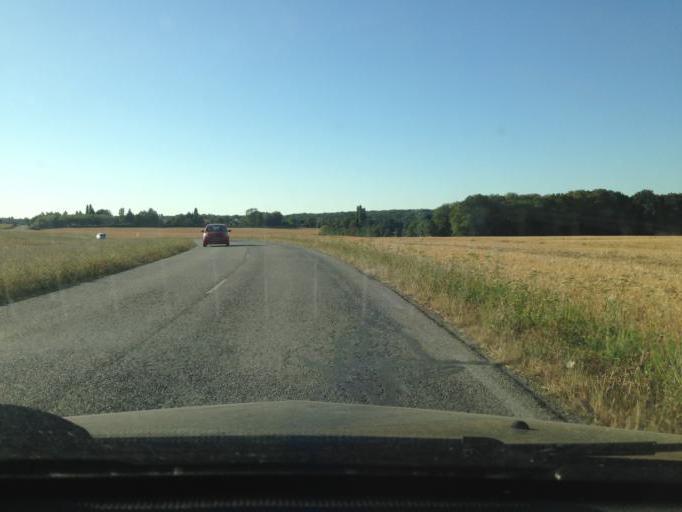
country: FR
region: Ile-de-France
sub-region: Departement des Yvelines
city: Magny-les-Hameaux
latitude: 48.7373
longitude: 2.0671
